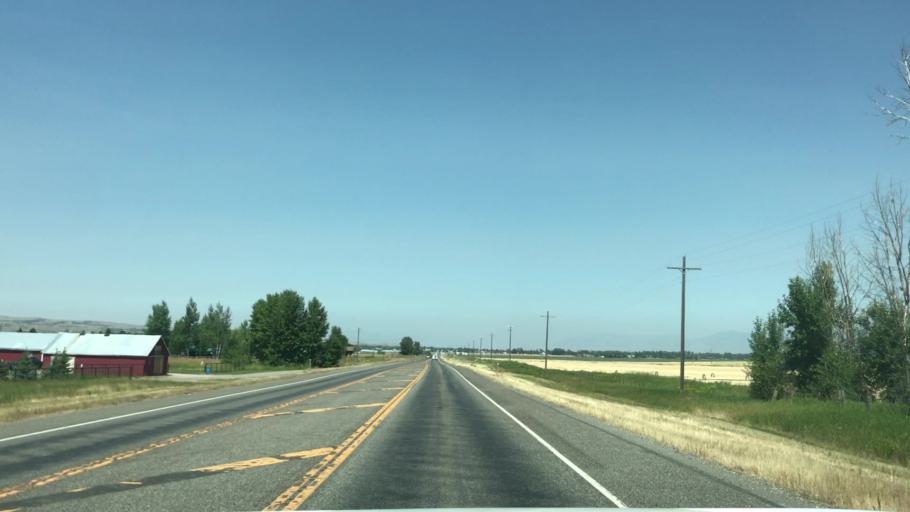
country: US
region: Montana
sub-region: Gallatin County
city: Four Corners
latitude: 45.5634
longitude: -111.1968
